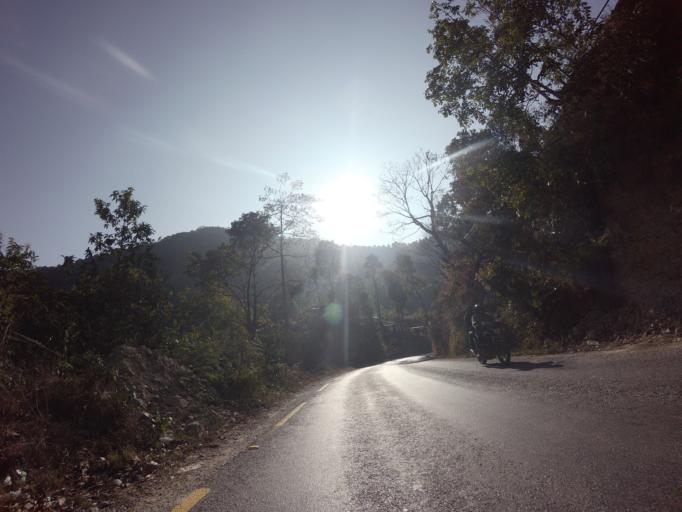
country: NP
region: Western Region
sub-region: Gandaki Zone
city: Pokhara
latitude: 28.1881
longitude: 83.9036
